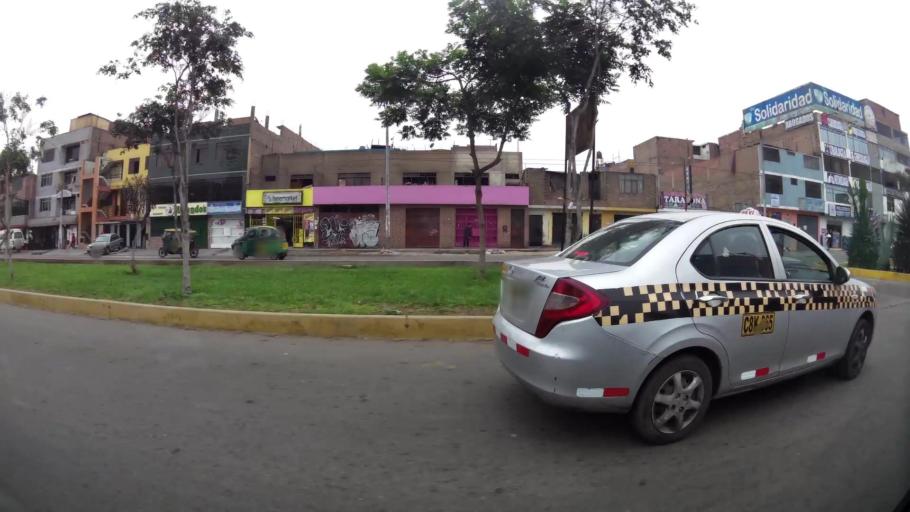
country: PE
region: Lima
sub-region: Lima
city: Independencia
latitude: -11.9723
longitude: -77.0732
